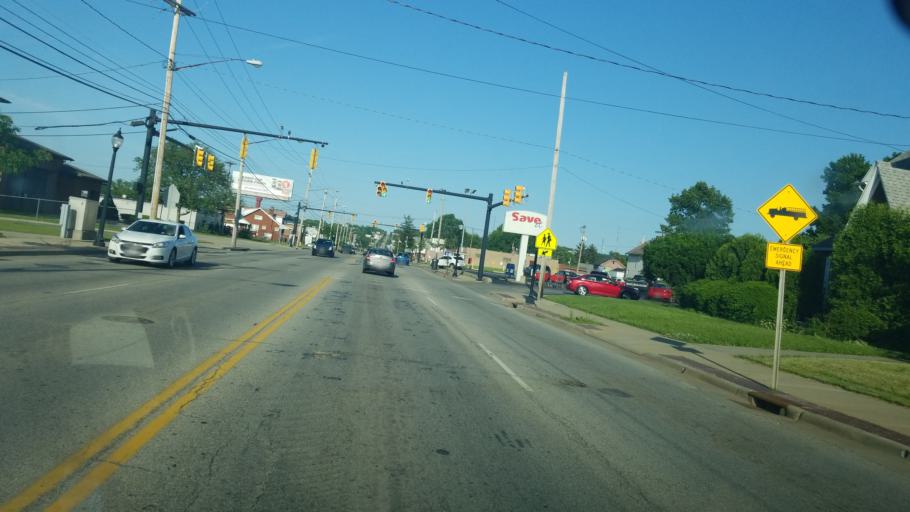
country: US
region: Ohio
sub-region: Summit County
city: Akron
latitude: 41.1023
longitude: -81.4968
